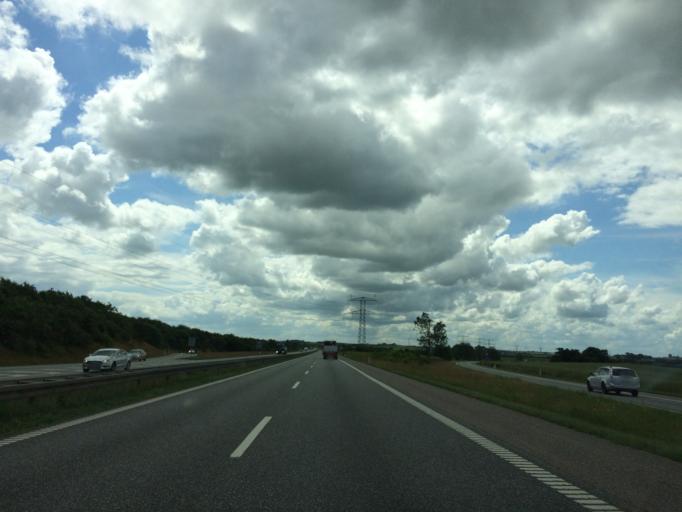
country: DK
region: North Denmark
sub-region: Rebild Kommune
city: Stovring
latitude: 56.8300
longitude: 9.7273
